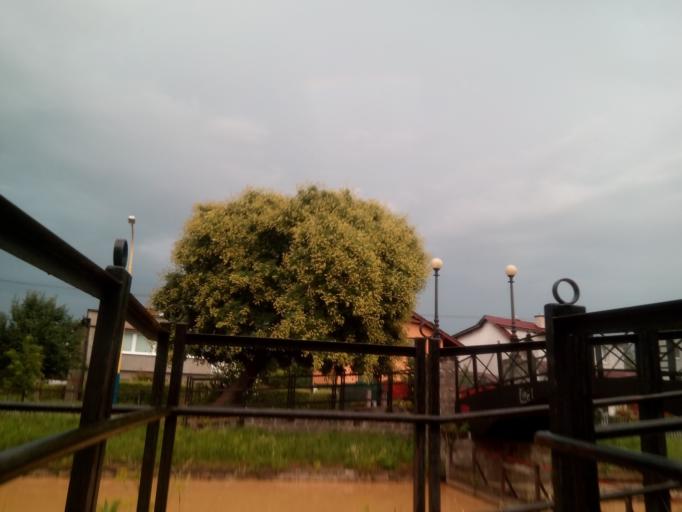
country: SK
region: Kosicky
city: Kosice
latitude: 48.7353
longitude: 21.2563
